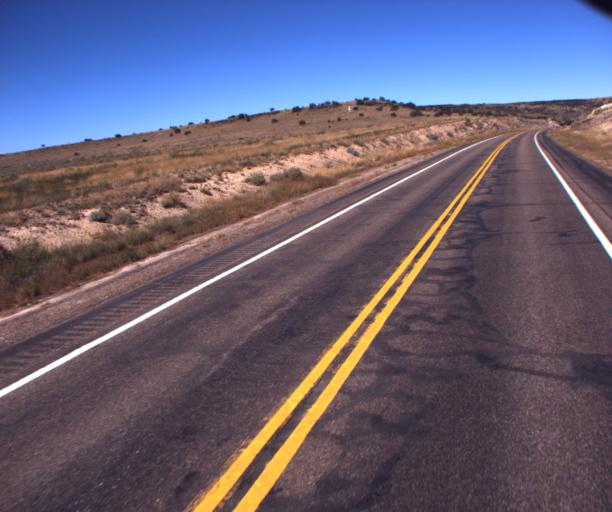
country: US
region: Arizona
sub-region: Apache County
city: Saint Johns
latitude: 34.3258
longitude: -109.3857
